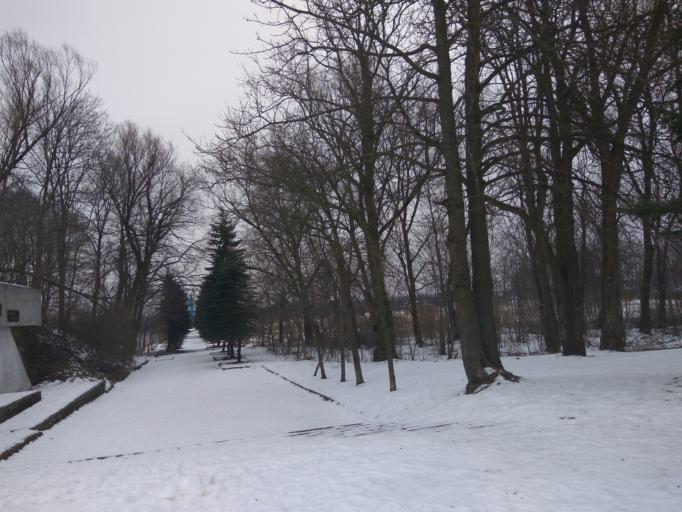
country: RU
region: Kaliningrad
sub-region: Gorod Kaliningrad
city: Kaliningrad
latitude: 54.7529
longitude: 20.4457
